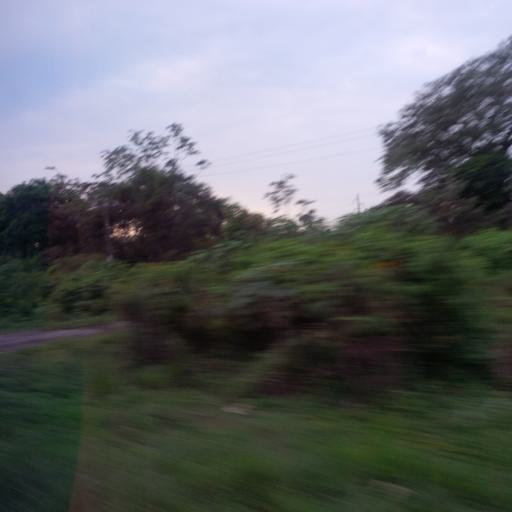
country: EC
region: Guayas
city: Coronel Marcelino Mariduena
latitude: -2.3289
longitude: -79.4186
